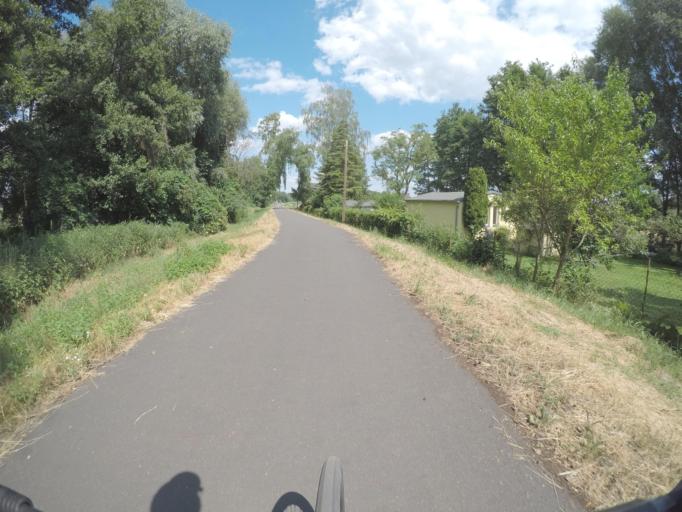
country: DE
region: Brandenburg
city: Roskow
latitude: 52.4302
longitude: 12.6484
